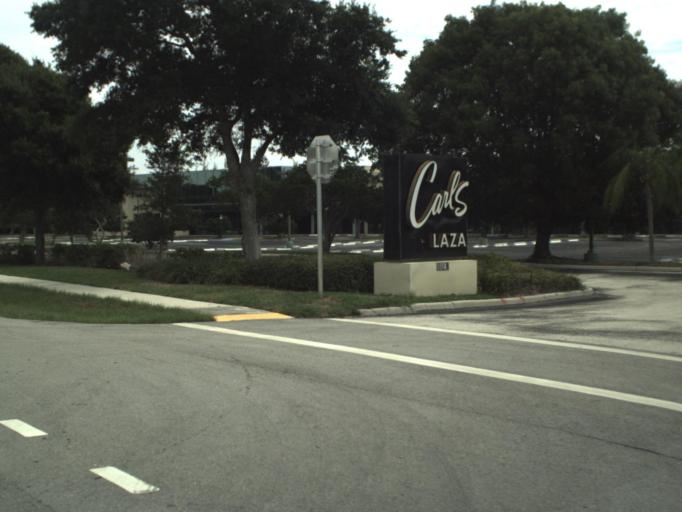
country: US
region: Florida
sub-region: Palm Beach County
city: Juno Beach
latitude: 26.8512
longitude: -80.0588
